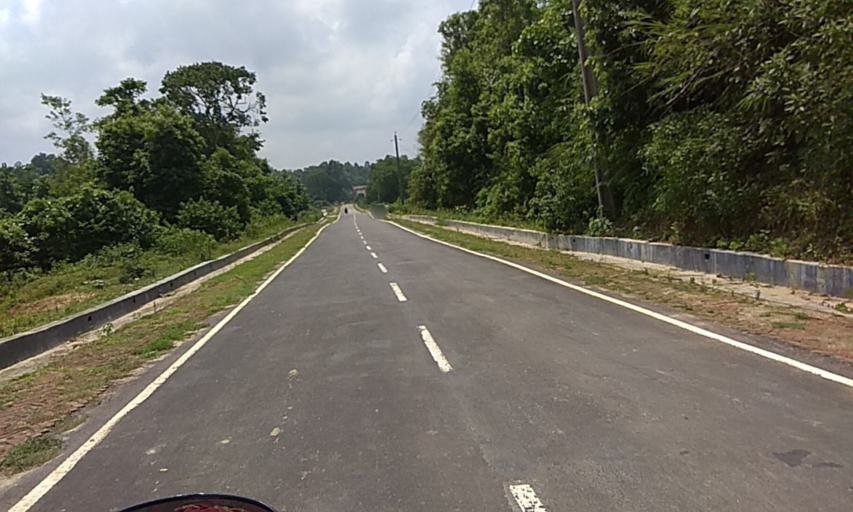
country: BD
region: Chittagong
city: Manikchari
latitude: 22.9368
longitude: 91.9069
